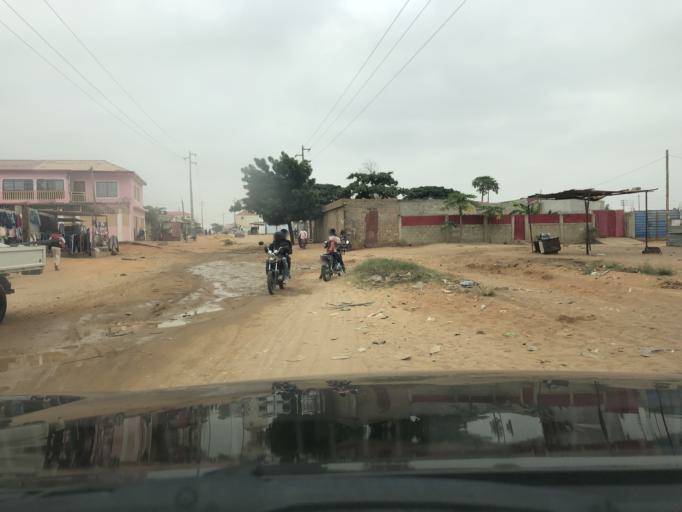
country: AO
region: Luanda
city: Luanda
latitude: -8.9389
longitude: 13.2393
